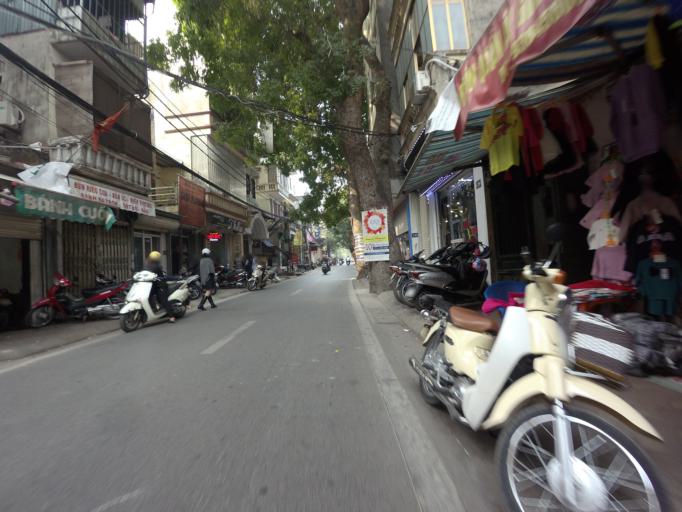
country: VN
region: Ha Noi
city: Hoan Kiem
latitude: 21.0539
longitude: 105.8359
